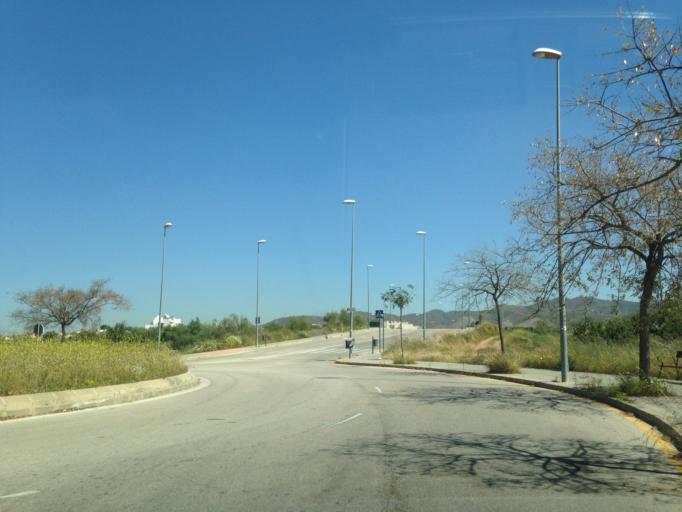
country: ES
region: Andalusia
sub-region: Provincia de Malaga
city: Malaga
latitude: 36.7322
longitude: -4.4892
